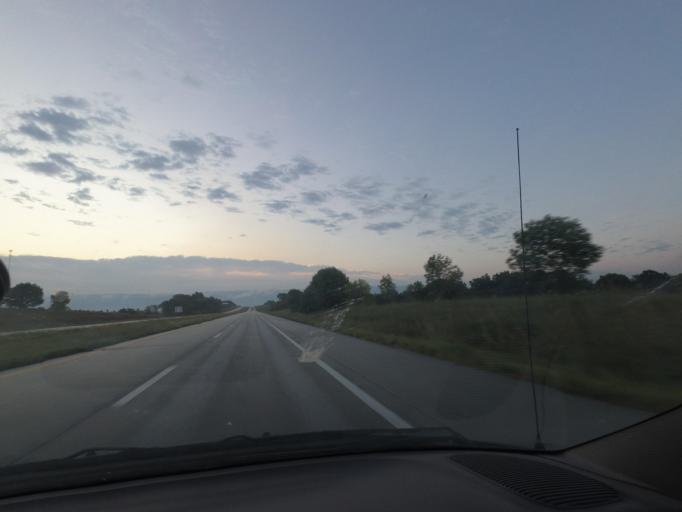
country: US
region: Missouri
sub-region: Macon County
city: Macon
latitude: 39.7569
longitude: -92.5442
